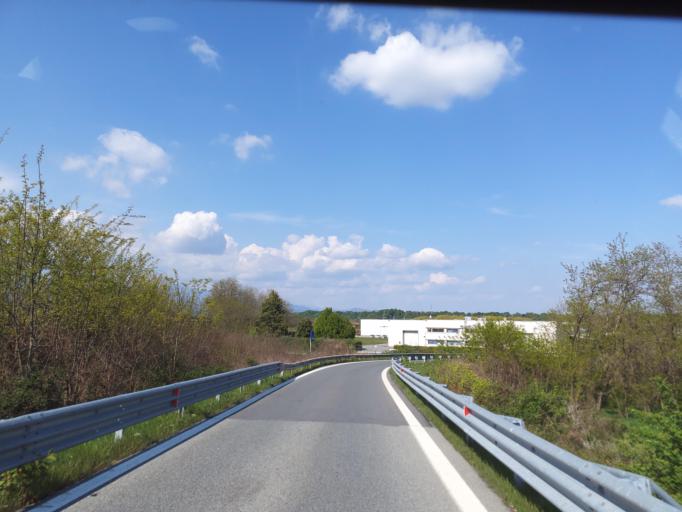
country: IT
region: Piedmont
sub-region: Provincia di Biella
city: Benna
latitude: 45.5013
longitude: 8.1293
